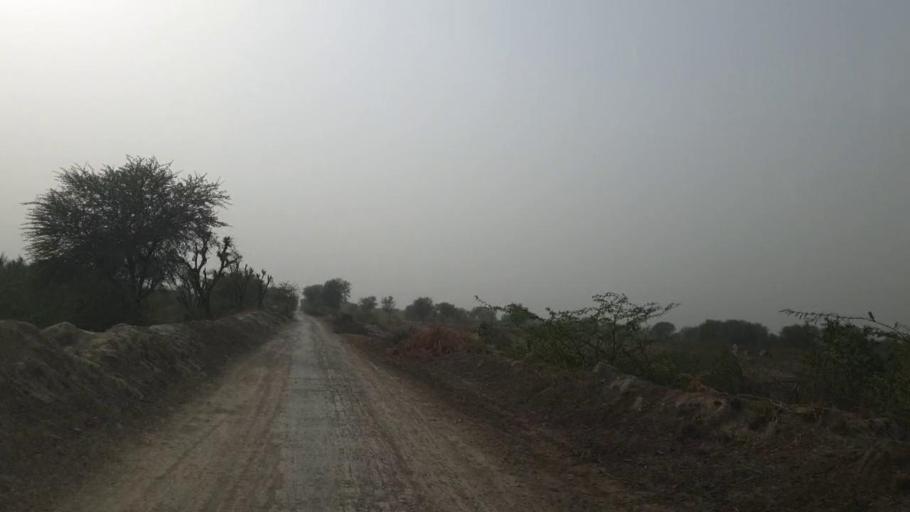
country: PK
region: Sindh
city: Kunri
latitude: 25.0678
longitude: 69.4905
